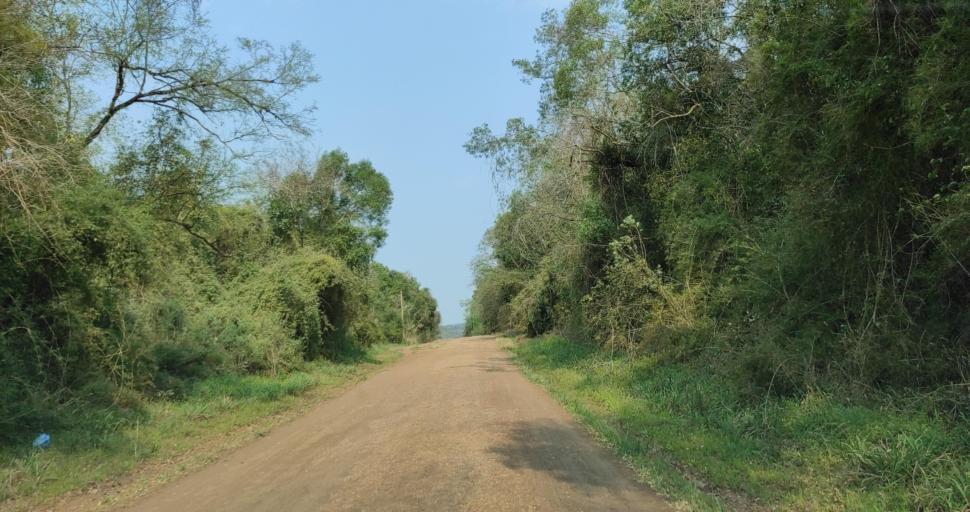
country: AR
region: Misiones
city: Cerro Cora
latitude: -27.5454
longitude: -55.5839
